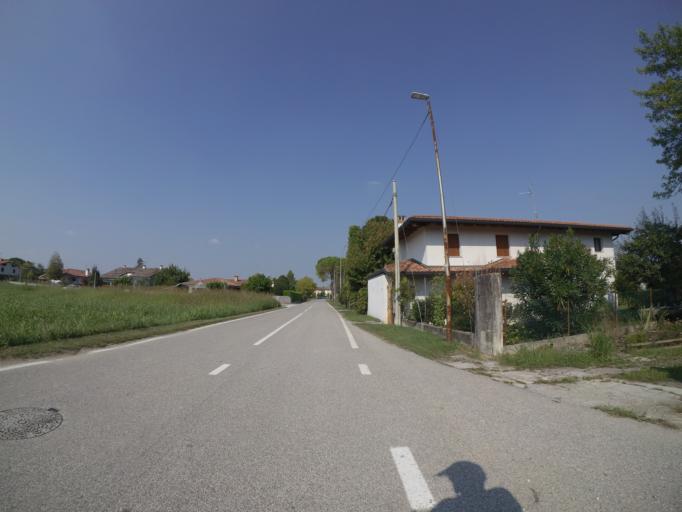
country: IT
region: Friuli Venezia Giulia
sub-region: Provincia di Udine
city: Varmo
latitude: 45.8900
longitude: 12.9598
